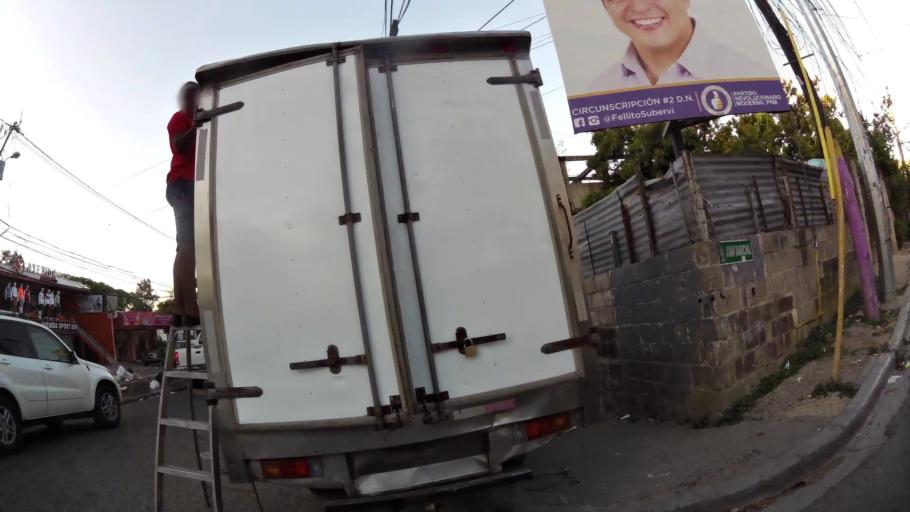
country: DO
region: Nacional
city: Santo Domingo
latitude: 18.4968
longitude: -69.9635
